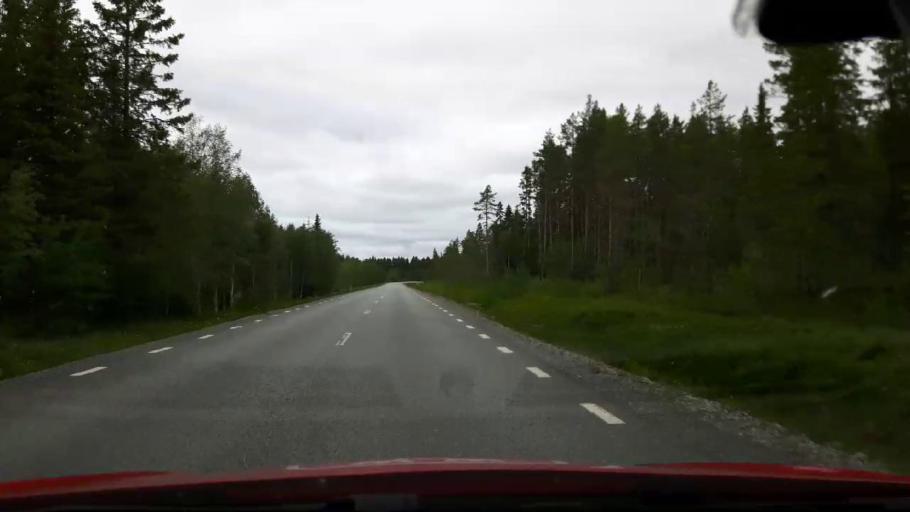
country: SE
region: Jaemtland
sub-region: OEstersunds Kommun
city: Lit
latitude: 63.6808
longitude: 14.6791
